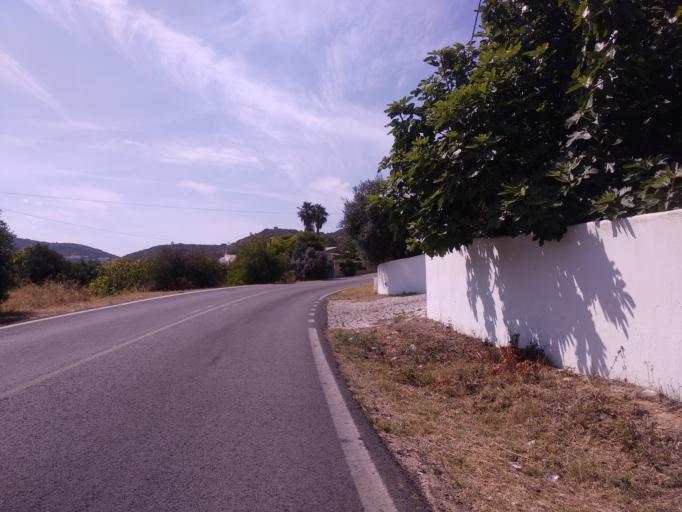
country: PT
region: Faro
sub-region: Faro
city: Santa Barbara de Nexe
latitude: 37.1118
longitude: -7.9618
